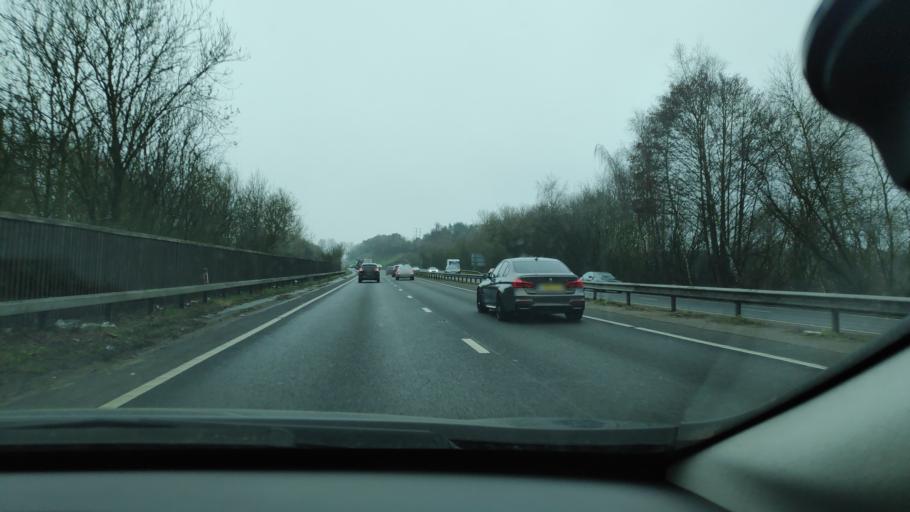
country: GB
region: England
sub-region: Hampshire
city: Aldershot
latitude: 51.2660
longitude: -0.7351
